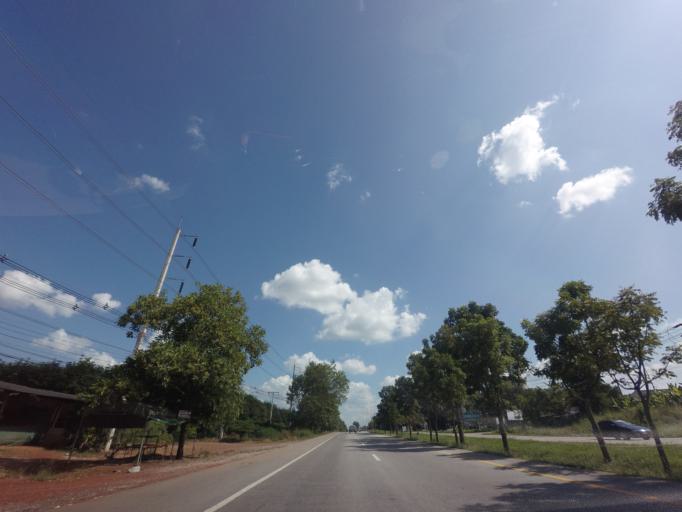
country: TH
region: Rayong
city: Wang Chan
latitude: 12.9613
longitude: 101.5030
